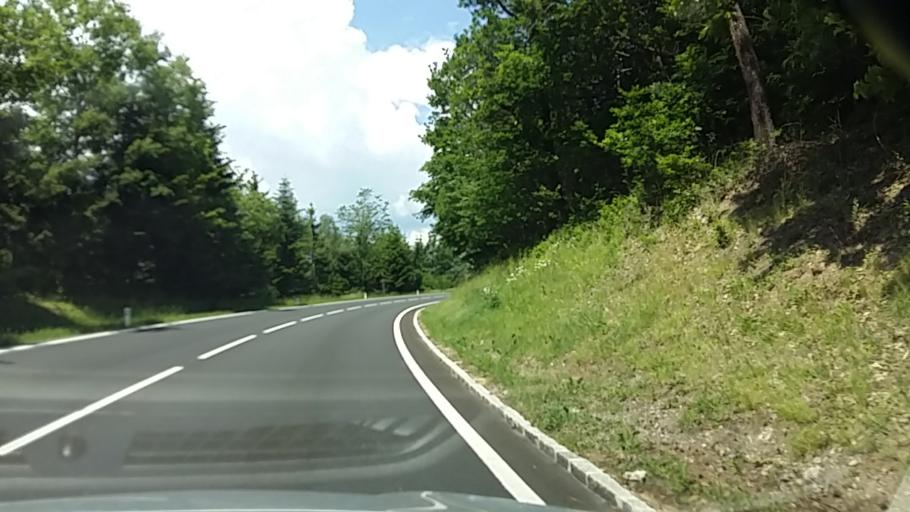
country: AT
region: Burgenland
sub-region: Politischer Bezirk Oberwart
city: Unterkohlstatten
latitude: 47.3993
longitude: 16.2915
